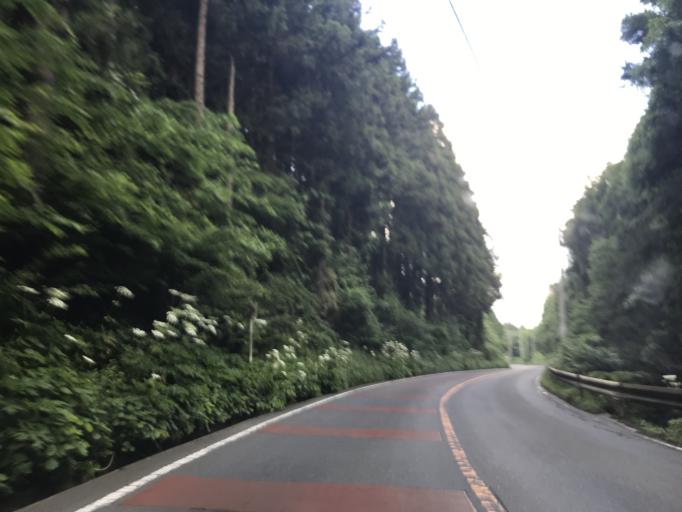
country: JP
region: Miyagi
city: Wakuya
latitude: 38.5760
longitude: 141.1445
